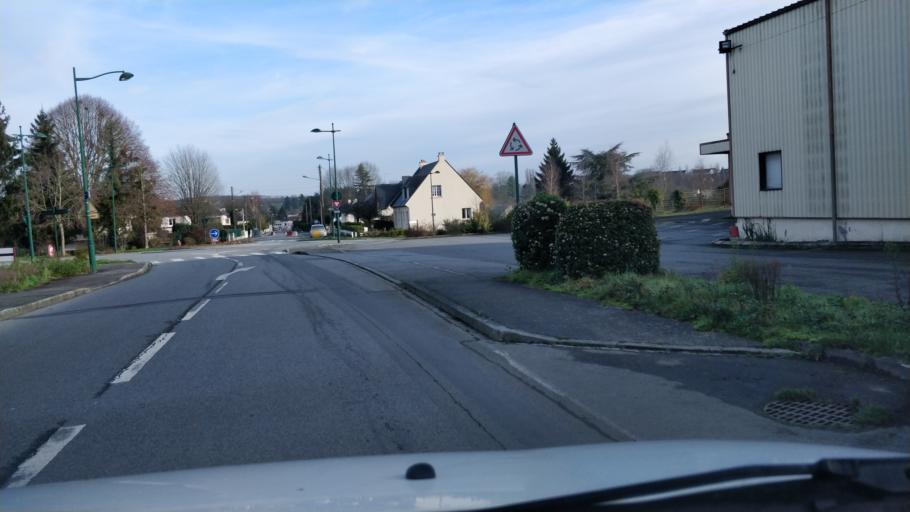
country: FR
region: Brittany
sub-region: Departement d'Ille-et-Vilaine
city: Argentre-du-Plessis
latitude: 48.0534
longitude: -1.1596
